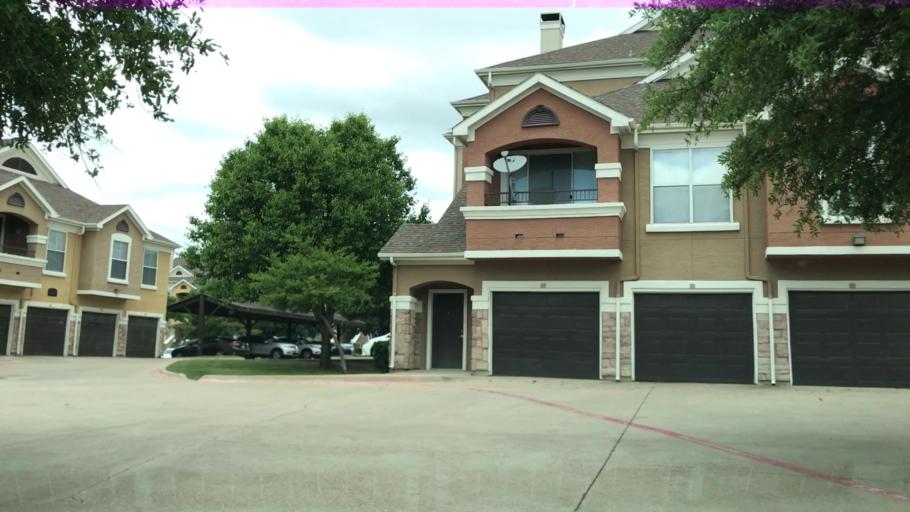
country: US
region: Texas
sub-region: Dallas County
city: Farmers Branch
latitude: 32.8918
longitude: -96.9559
